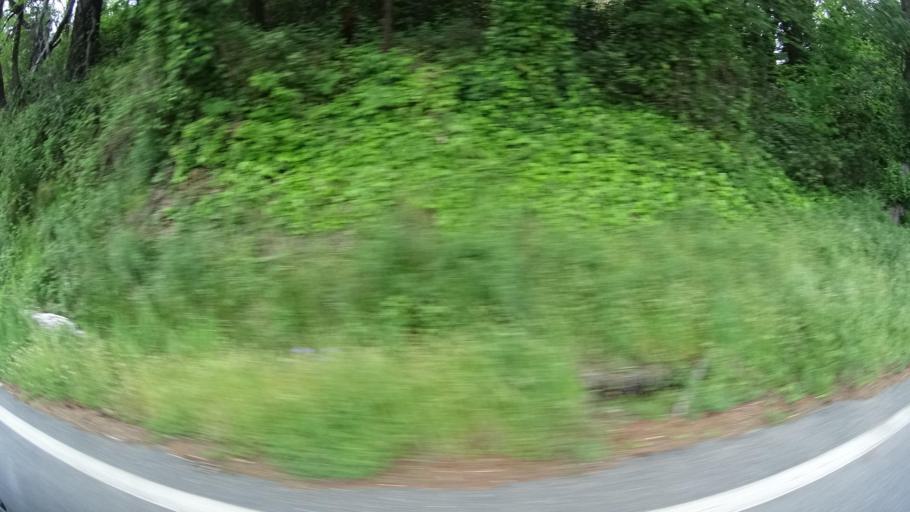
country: US
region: California
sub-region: Humboldt County
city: Willow Creek
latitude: 41.2969
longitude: -123.5596
